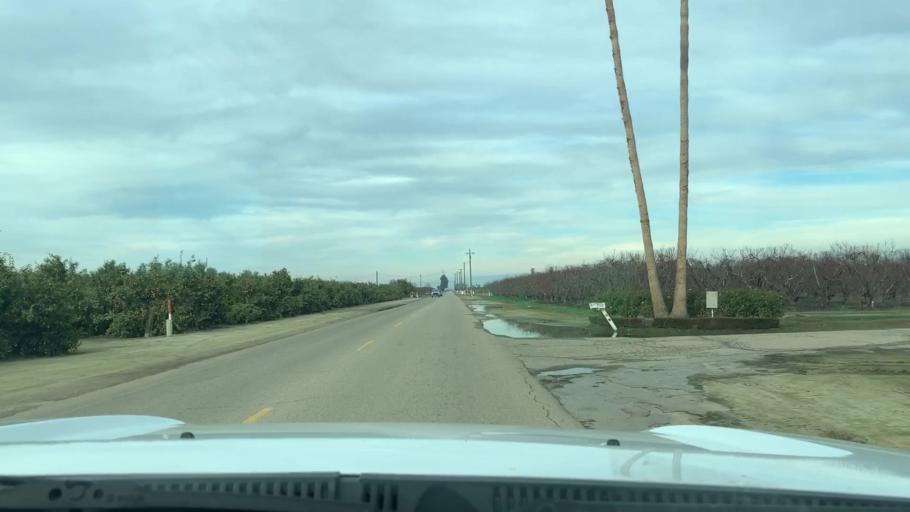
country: US
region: California
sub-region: Fresno County
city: Parlier
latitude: 36.6106
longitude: -119.5748
